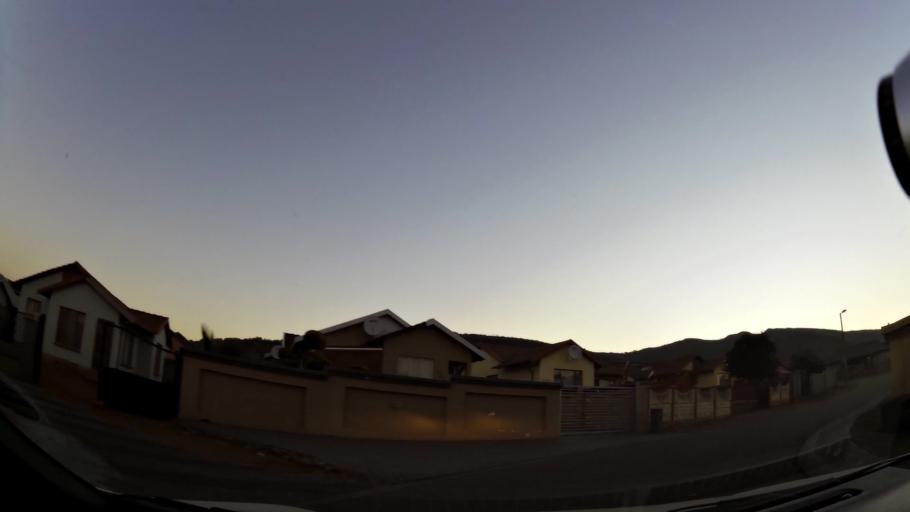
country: ZA
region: North-West
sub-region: Bojanala Platinum District Municipality
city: Rustenburg
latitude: -25.6576
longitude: 27.2051
